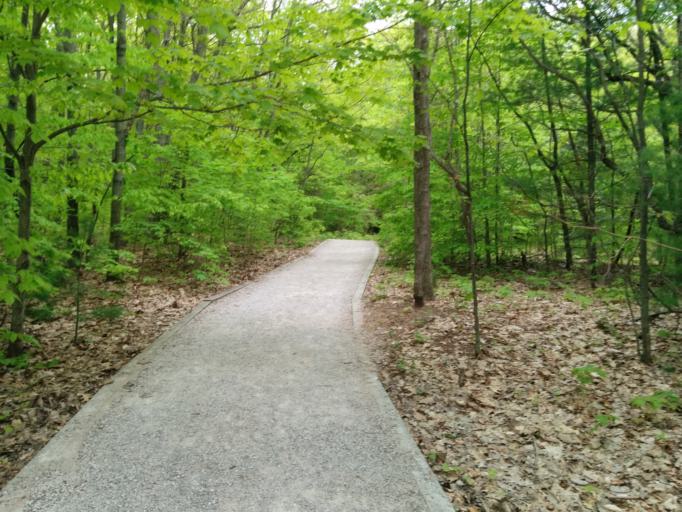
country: US
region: Michigan
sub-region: Ottawa County
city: Grand Haven
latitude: 43.0206
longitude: -86.2229
